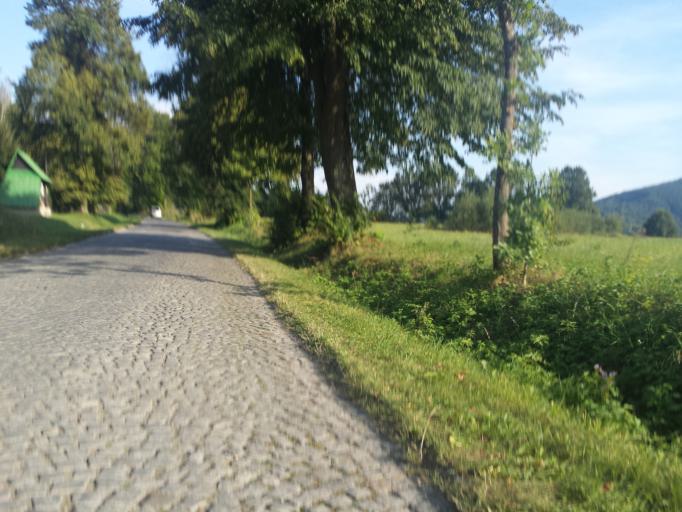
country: PL
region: Subcarpathian Voivodeship
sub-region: Powiat leski
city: Uherce Mineralne
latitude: 49.4454
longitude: 22.3947
